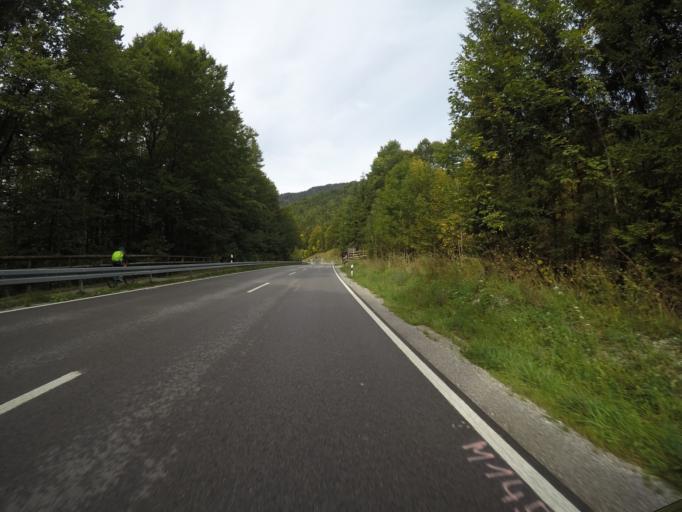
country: DE
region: Bavaria
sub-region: Upper Bavaria
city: Lenggries
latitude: 47.5842
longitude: 11.6034
